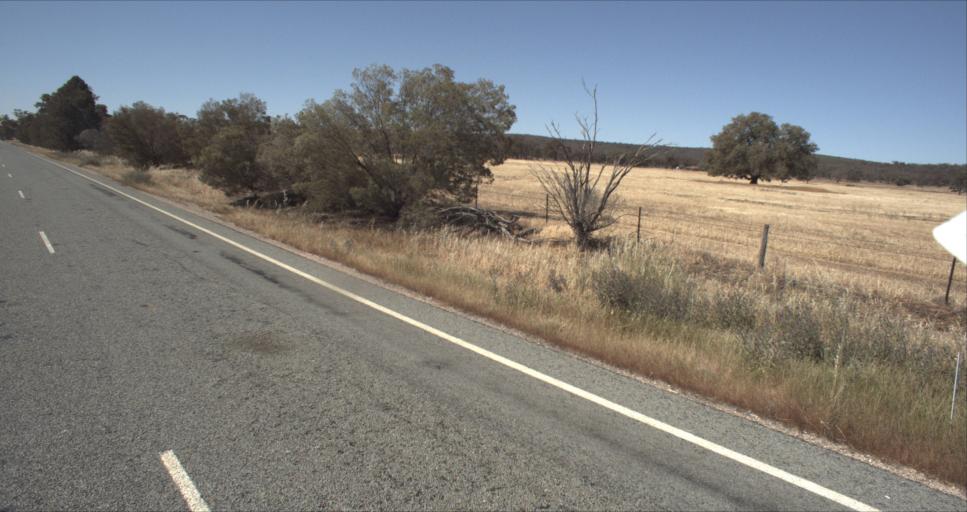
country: AU
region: New South Wales
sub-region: Leeton
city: Leeton
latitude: -34.4646
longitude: 146.4371
